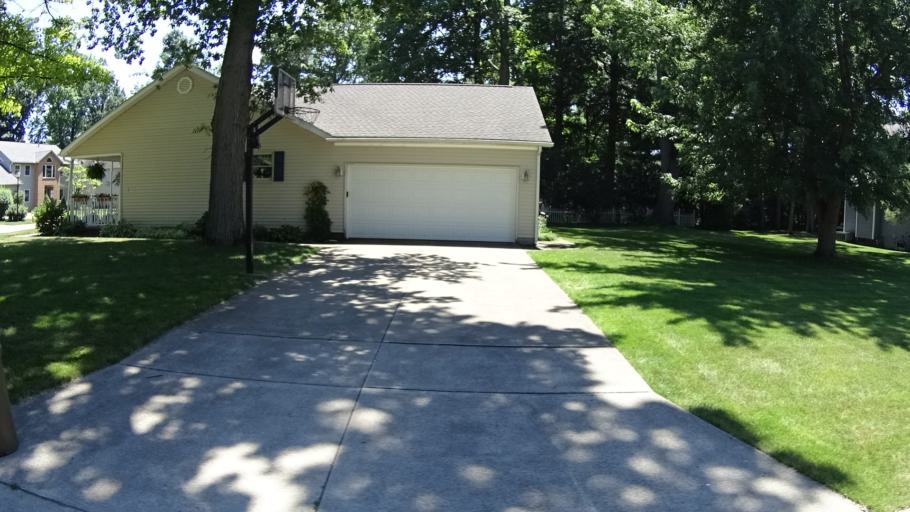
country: US
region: Ohio
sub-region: Erie County
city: Huron
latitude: 41.3938
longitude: -82.5692
